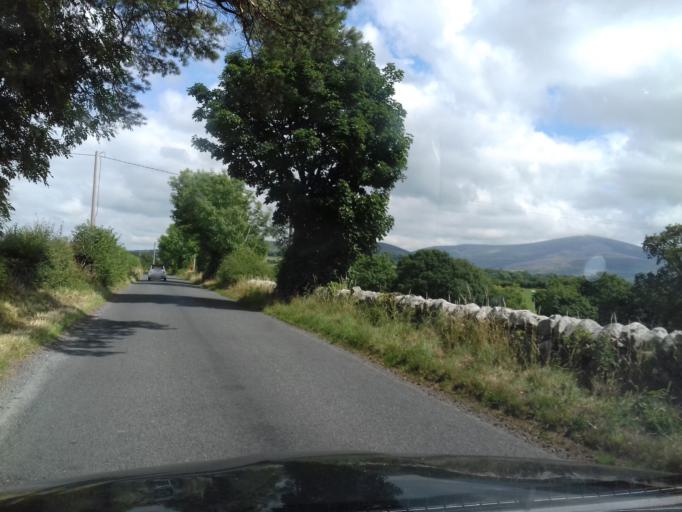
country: IE
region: Leinster
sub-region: Kilkenny
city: Graiguenamanagh
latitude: 52.6072
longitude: -6.9029
